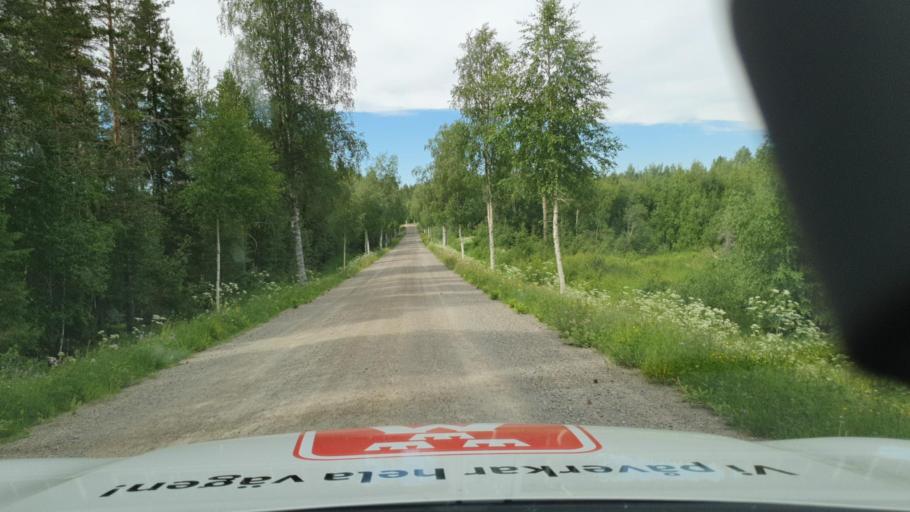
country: SE
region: Vaesterbotten
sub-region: Skelleftea Kommun
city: Burtraesk
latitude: 64.4760
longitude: 20.4432
